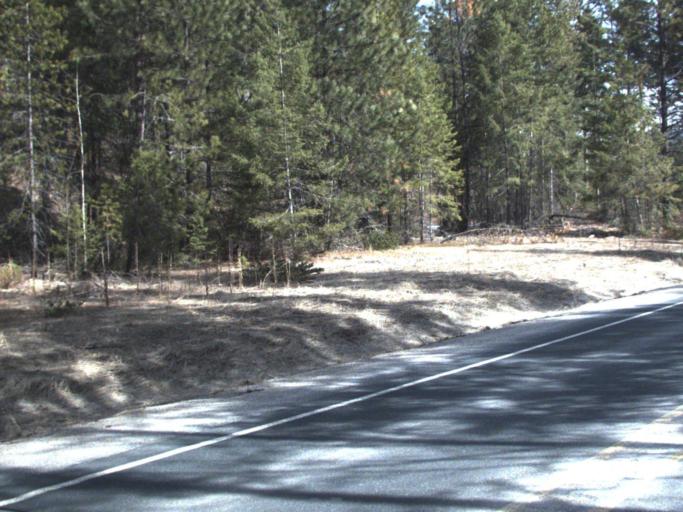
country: US
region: Washington
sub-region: Stevens County
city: Chewelah
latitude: 48.5055
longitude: -117.6661
